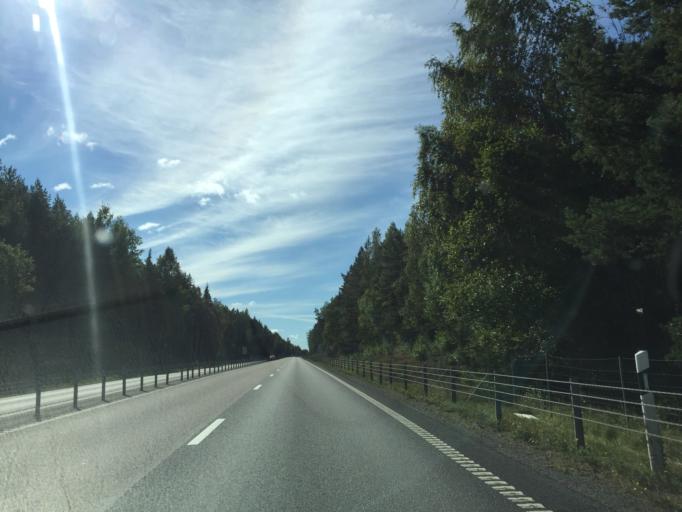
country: SE
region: Vaestmanland
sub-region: Kopings Kommun
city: Koping
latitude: 59.5468
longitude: 16.0135
